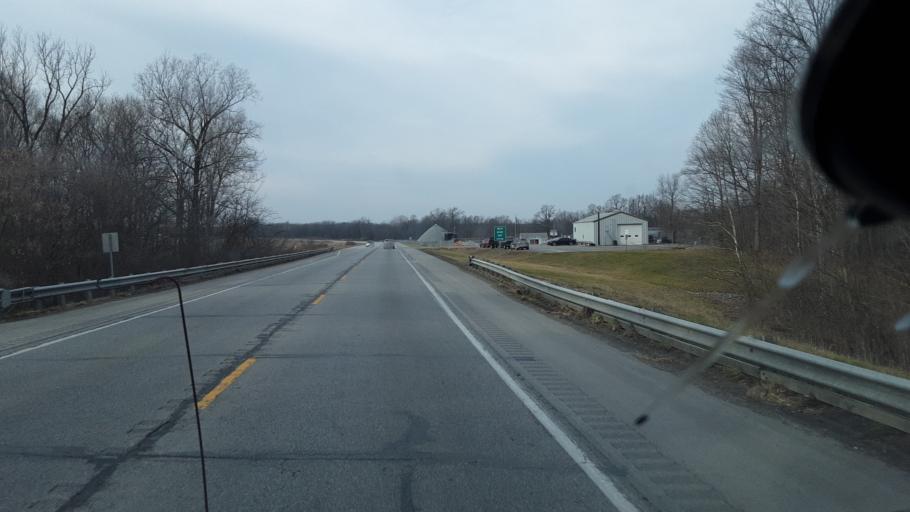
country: US
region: Indiana
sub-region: DeKalb County
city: Waterloo
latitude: 41.4362
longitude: -85.0335
